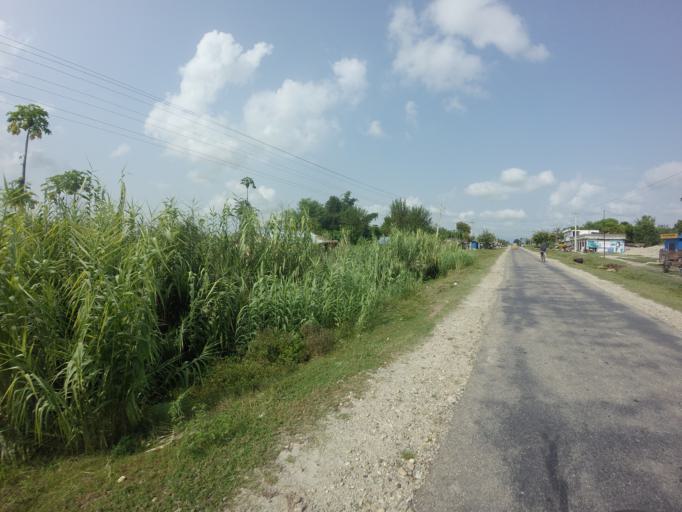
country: NP
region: Far Western
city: Tikapur
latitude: 28.4733
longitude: 81.0717
